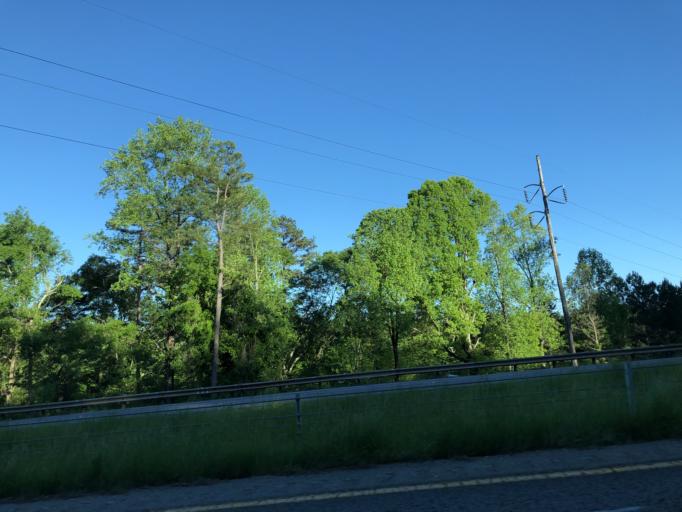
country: US
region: Georgia
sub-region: Clarke County
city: Country Club Estates
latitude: 33.9545
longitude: -83.4390
